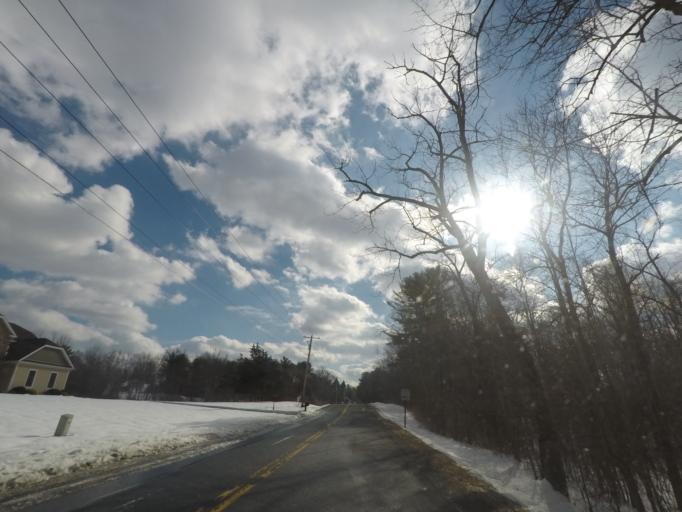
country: US
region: New York
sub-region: Schenectady County
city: Niskayuna
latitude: 42.8397
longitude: -73.8743
